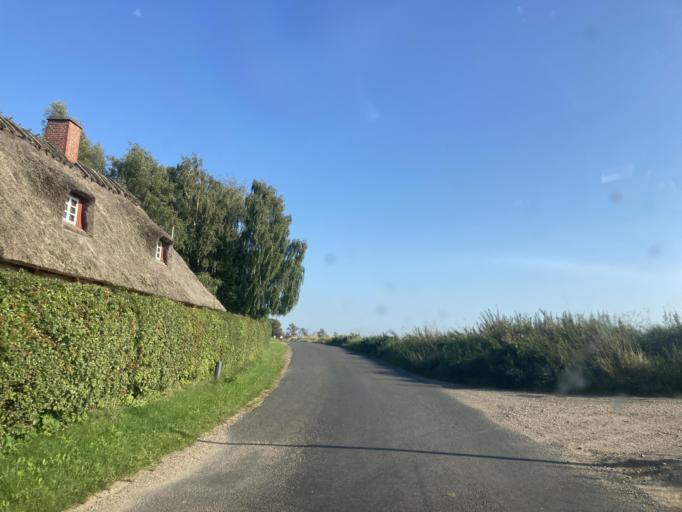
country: DK
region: South Denmark
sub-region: Svendborg Kommune
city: Thuro By
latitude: 55.1149
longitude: 10.7335
